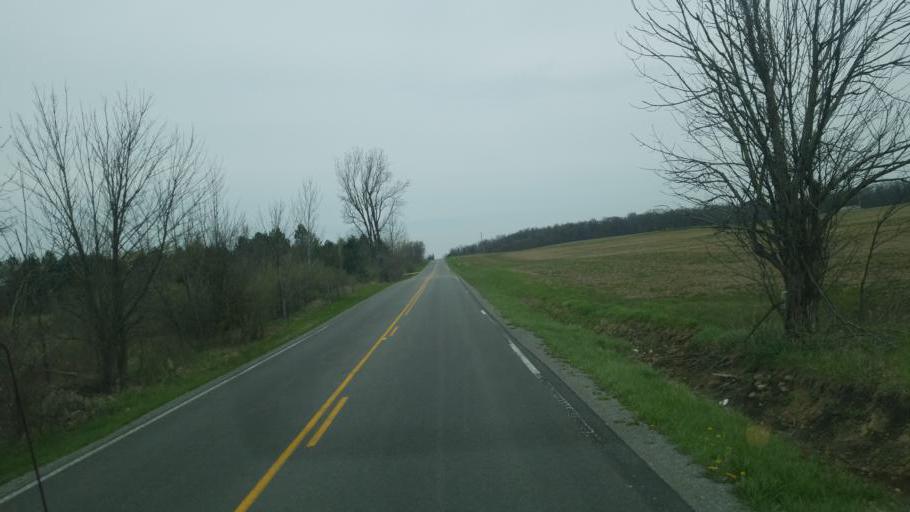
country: US
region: Ohio
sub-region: Seneca County
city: Fostoria
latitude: 41.0428
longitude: -83.4774
